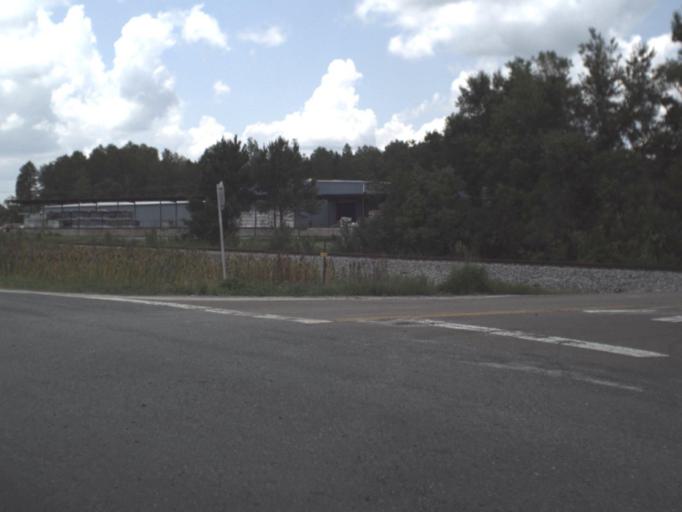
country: US
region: Florida
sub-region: Columbia County
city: Five Points
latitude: 30.2075
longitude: -82.6477
